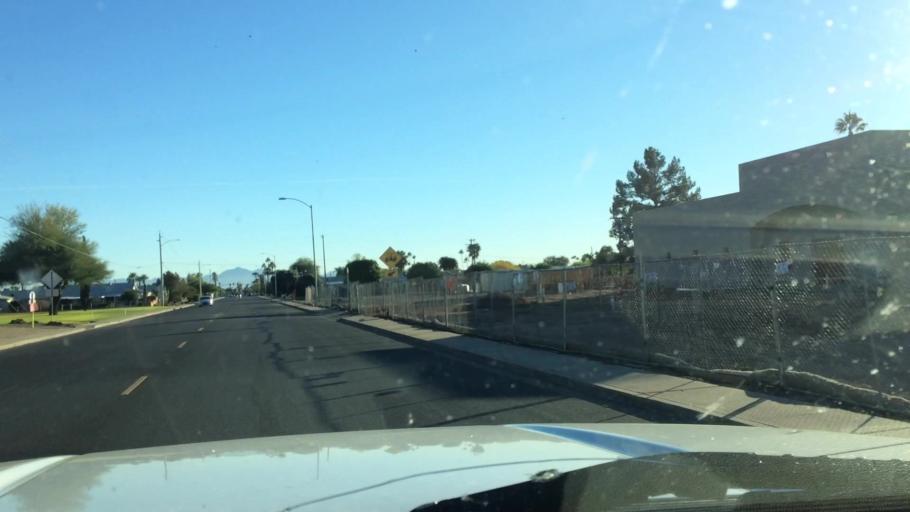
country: US
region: Arizona
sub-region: Maricopa County
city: Sun City
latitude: 33.5843
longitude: -112.2813
